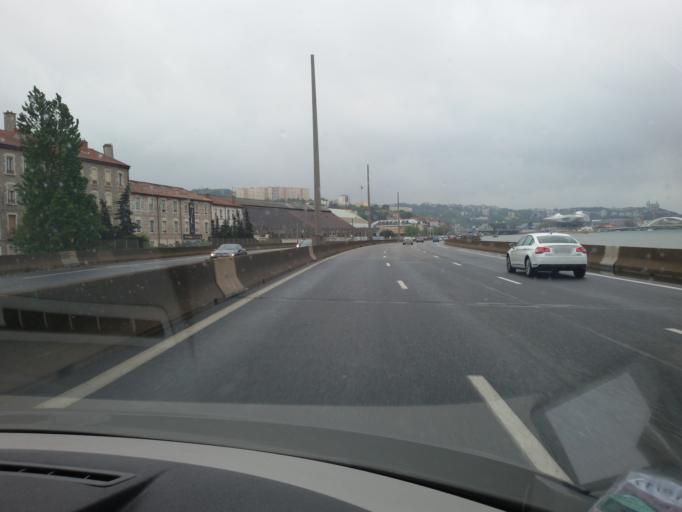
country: FR
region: Rhone-Alpes
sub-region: Departement du Rhone
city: La Mulatiere
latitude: 45.7188
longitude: 4.8190
